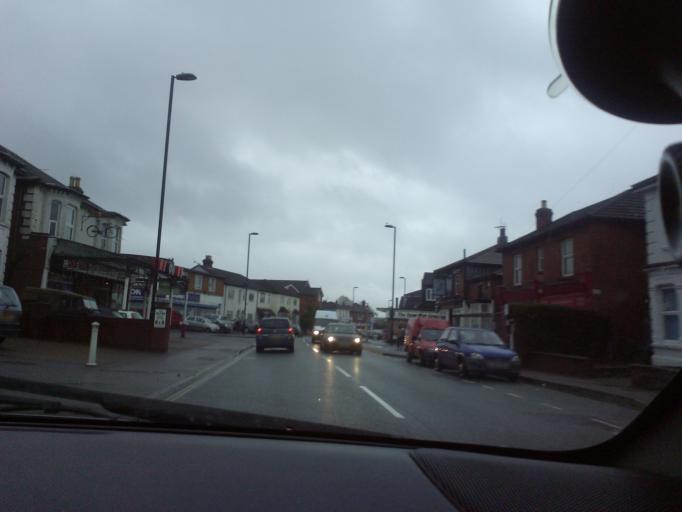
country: GB
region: England
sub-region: Southampton
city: Southampton
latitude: 50.9125
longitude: -1.4212
